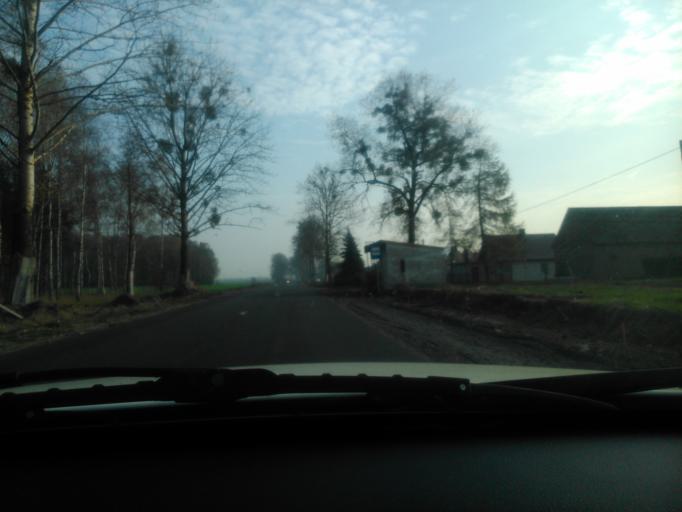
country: PL
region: Warmian-Masurian Voivodeship
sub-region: Powiat dzialdowski
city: Lidzbark
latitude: 53.2473
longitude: 19.9166
